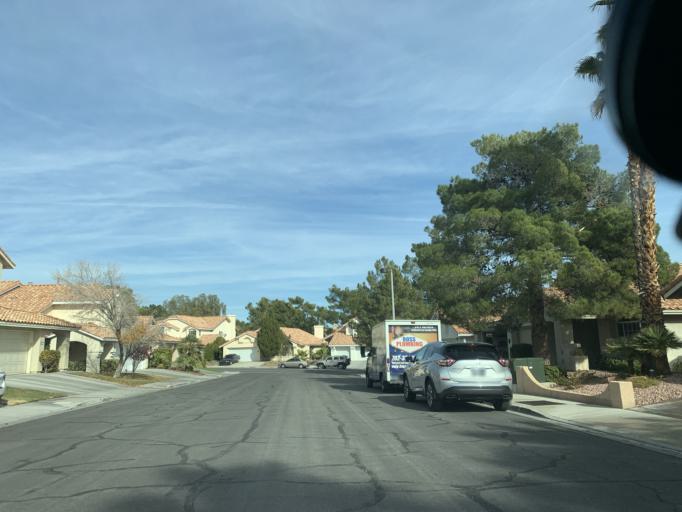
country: US
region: Nevada
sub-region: Clark County
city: Summerlin South
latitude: 36.1493
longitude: -115.3026
